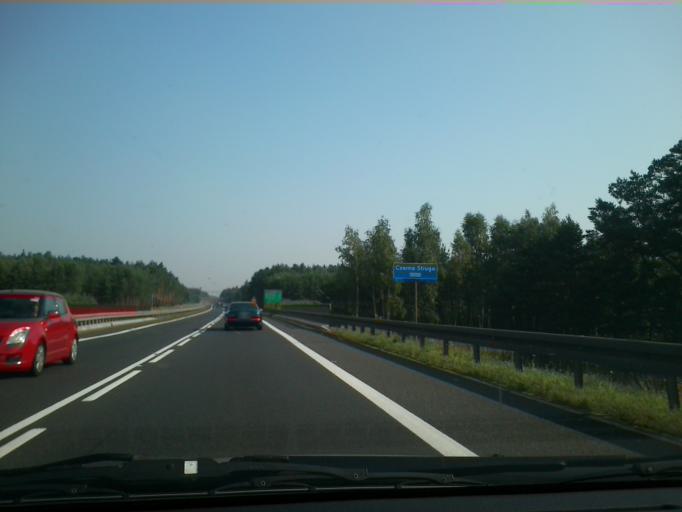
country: PL
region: Lubusz
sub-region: Powiat nowosolski
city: Nowa Sol
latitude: 51.8015
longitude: 15.6770
